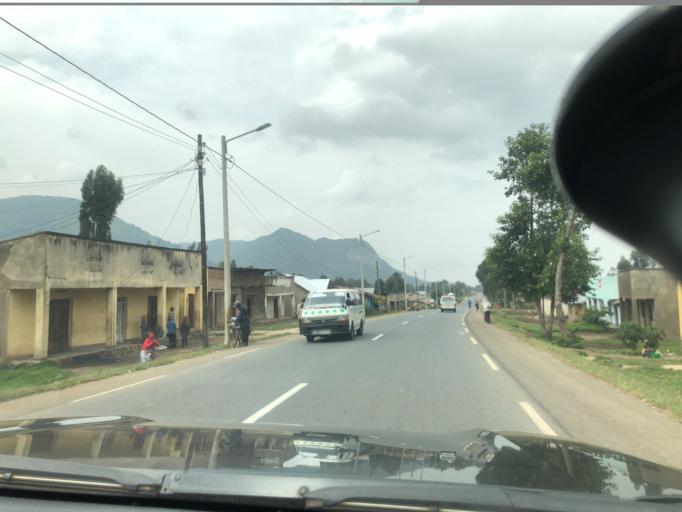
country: RW
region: Western Province
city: Gisenyi
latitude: -1.6338
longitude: 29.4116
